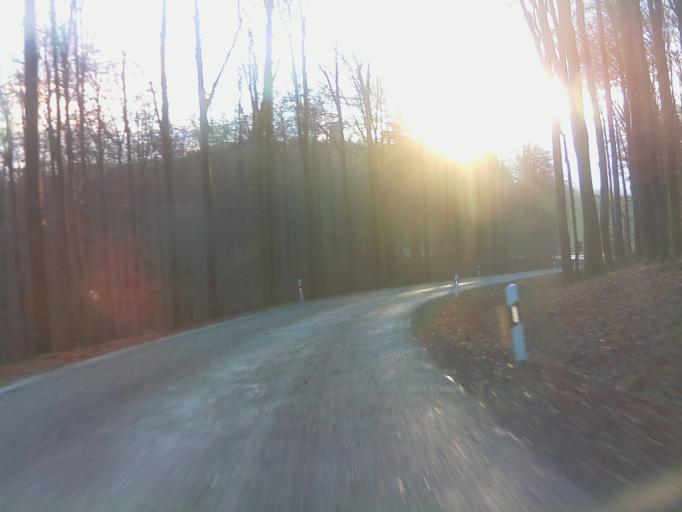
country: DE
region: Bavaria
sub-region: Regierungsbezirk Unterfranken
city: Hausen
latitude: 50.4845
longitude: 10.0952
